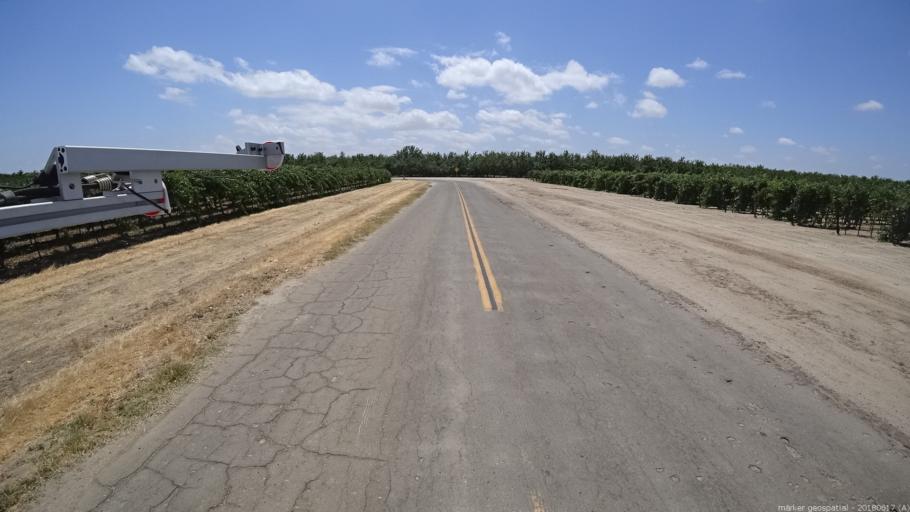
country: US
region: California
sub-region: Fresno County
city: Kerman
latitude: 36.8263
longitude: -120.2113
